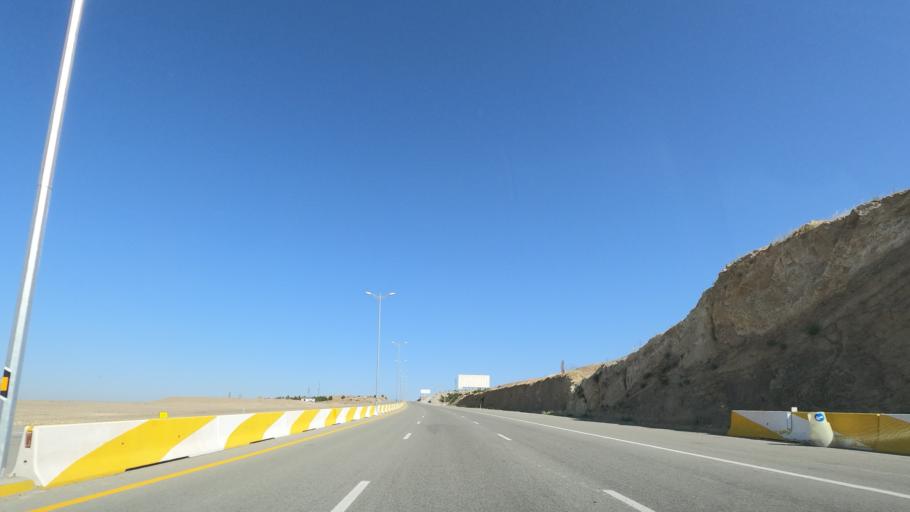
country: IR
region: Tehran
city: Shahr-e Qods
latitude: 35.7621
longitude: 51.0736
